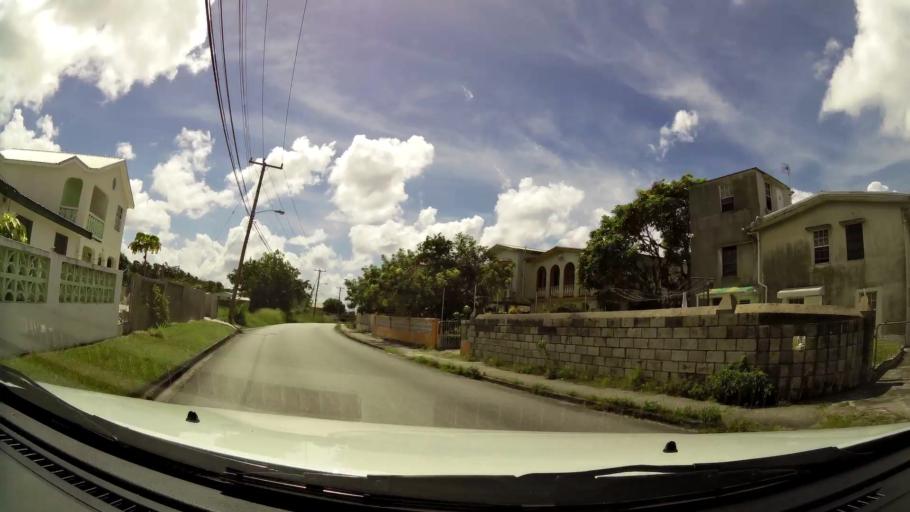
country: BB
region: Saint James
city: Holetown
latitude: 13.1477
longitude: -59.6299
